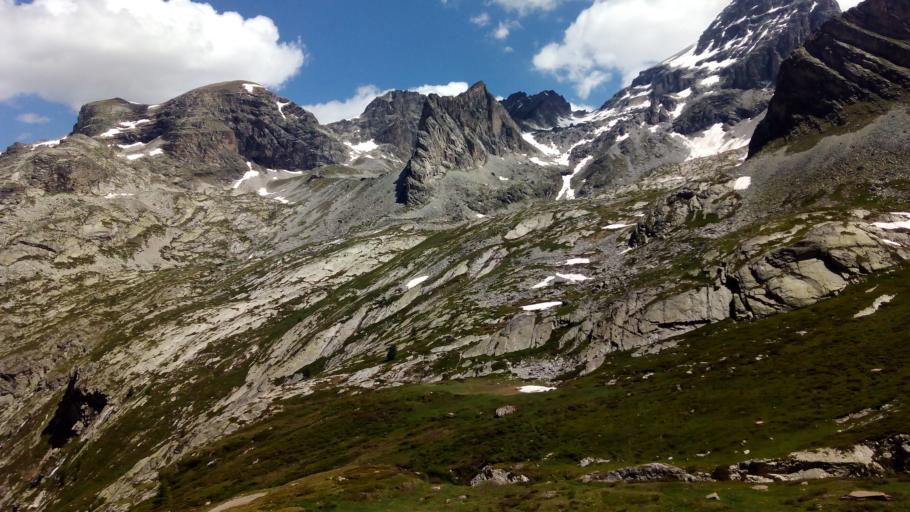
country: IT
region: Piedmont
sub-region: Provincia di Torino
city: Oulx
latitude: 45.1266
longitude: 6.8038
